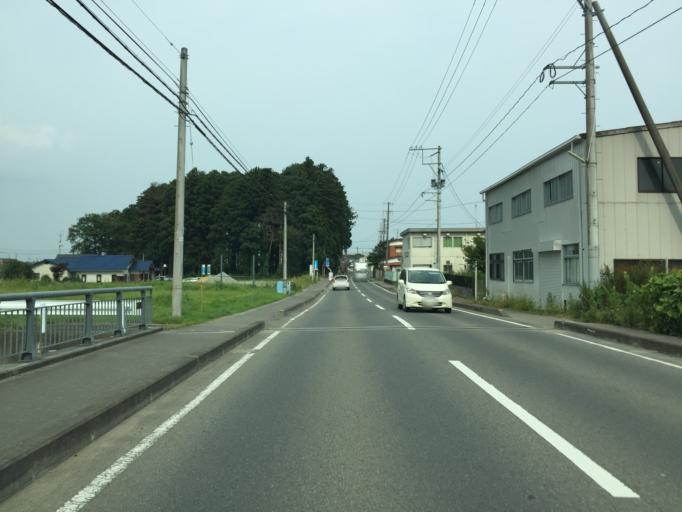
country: JP
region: Fukushima
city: Namie
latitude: 37.6361
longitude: 140.9454
